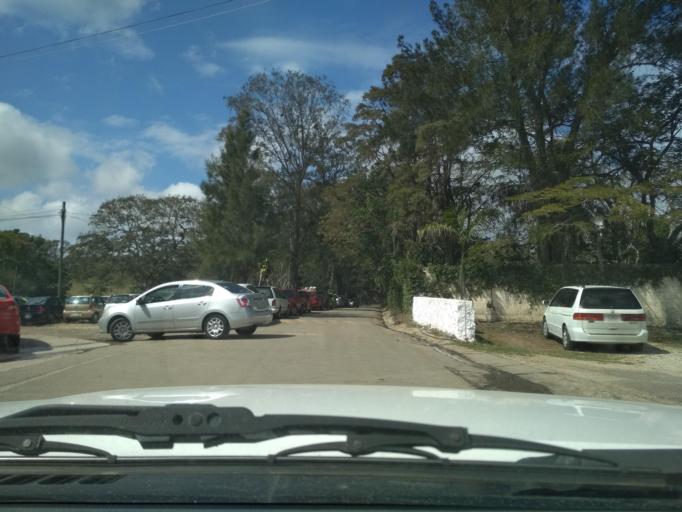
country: MX
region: Veracruz
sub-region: Emiliano Zapata
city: Dos Rios
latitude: 19.4851
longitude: -96.8134
